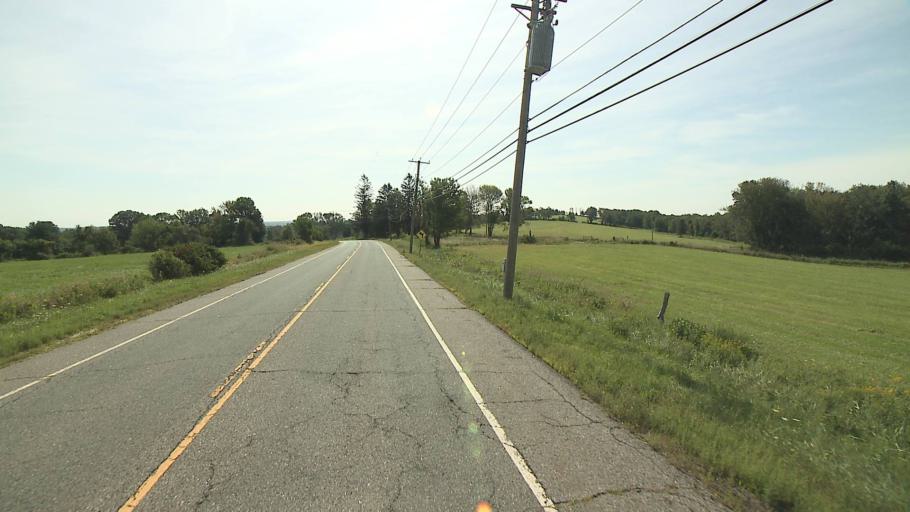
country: US
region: Connecticut
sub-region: Litchfield County
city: Thomaston
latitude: 41.7065
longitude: -73.1308
